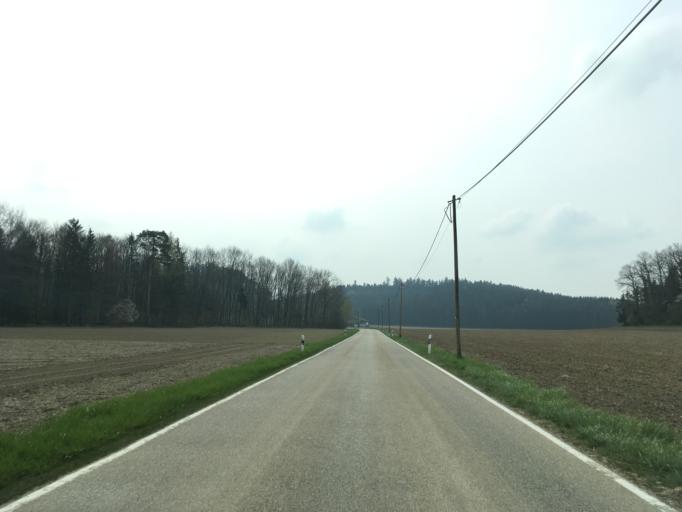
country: DE
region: Bavaria
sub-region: Upper Bavaria
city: Jettenbach
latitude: 48.1609
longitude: 12.3795
